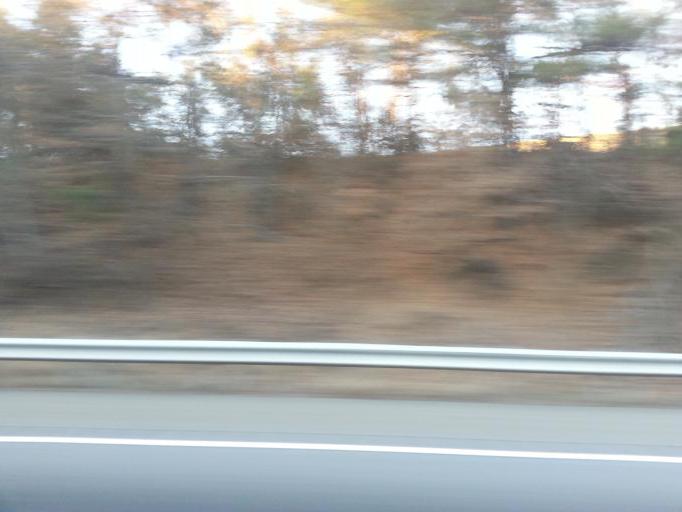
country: US
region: North Carolina
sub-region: Buncombe County
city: Bent Creek
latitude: 35.5539
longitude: -82.6898
